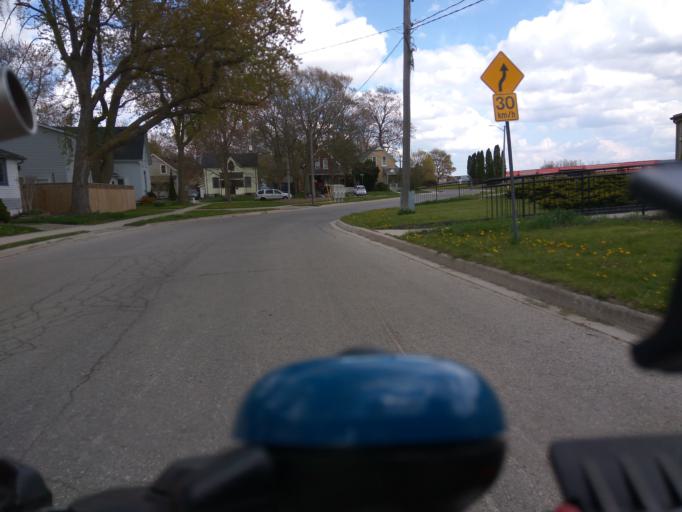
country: CA
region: Ontario
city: Stratford
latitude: 43.3656
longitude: -80.9734
